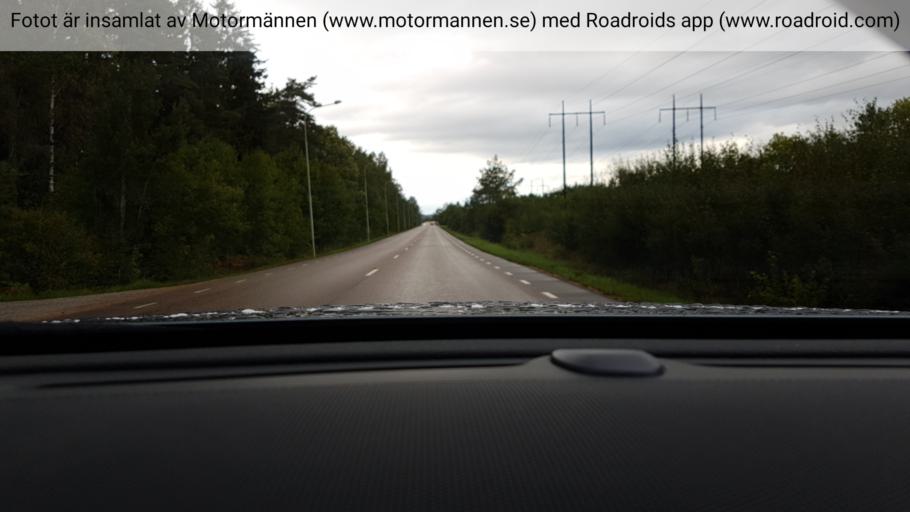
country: SE
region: Vaestra Goetaland
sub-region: Vanersborgs Kommun
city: Vanersborg
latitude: 58.3485
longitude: 12.3481
